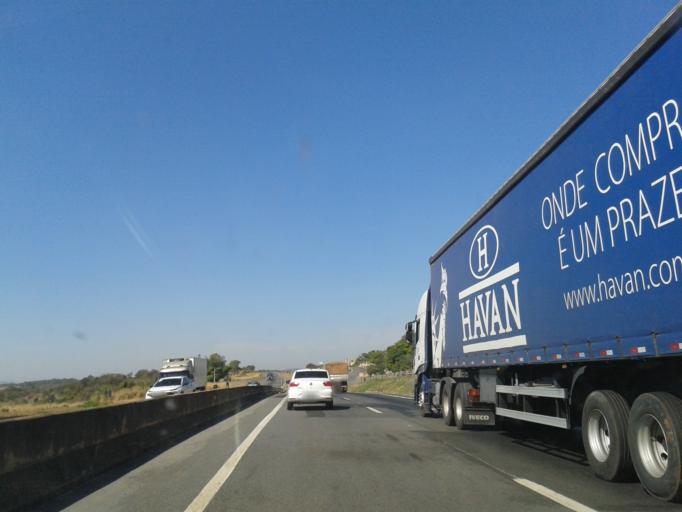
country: BR
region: Goias
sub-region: Piracanjuba
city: Piracanjuba
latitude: -17.2521
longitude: -49.2418
